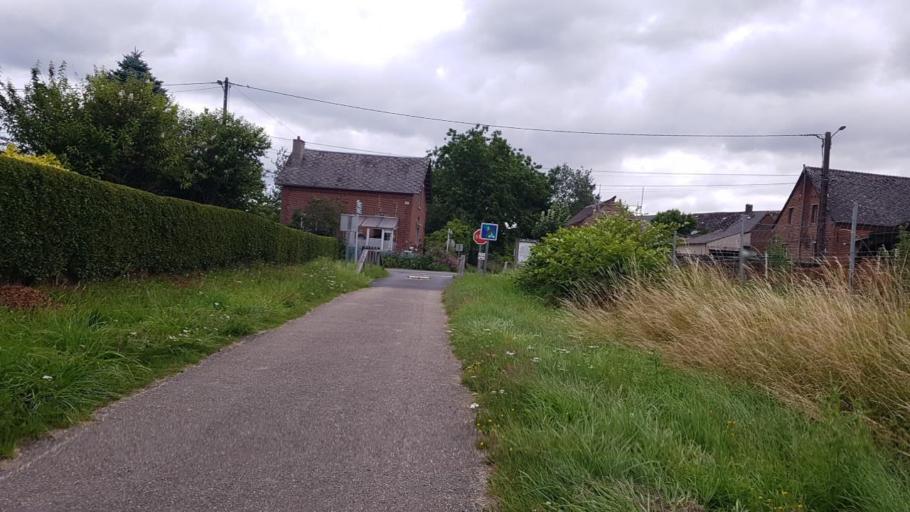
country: FR
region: Picardie
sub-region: Departement de l'Aisne
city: Buironfosse
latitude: 49.9067
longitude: 3.7917
